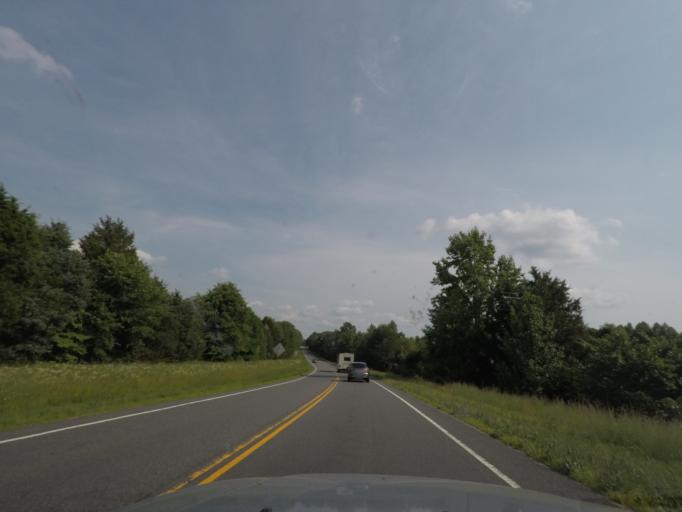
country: US
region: Virginia
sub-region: Buckingham County
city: Buckingham
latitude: 37.5194
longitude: -78.4947
